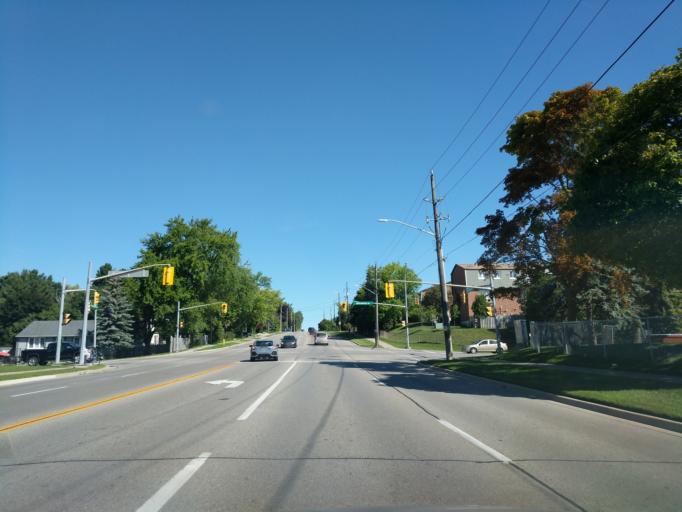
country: CA
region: Ontario
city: Ajax
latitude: 43.8385
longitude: -79.0916
